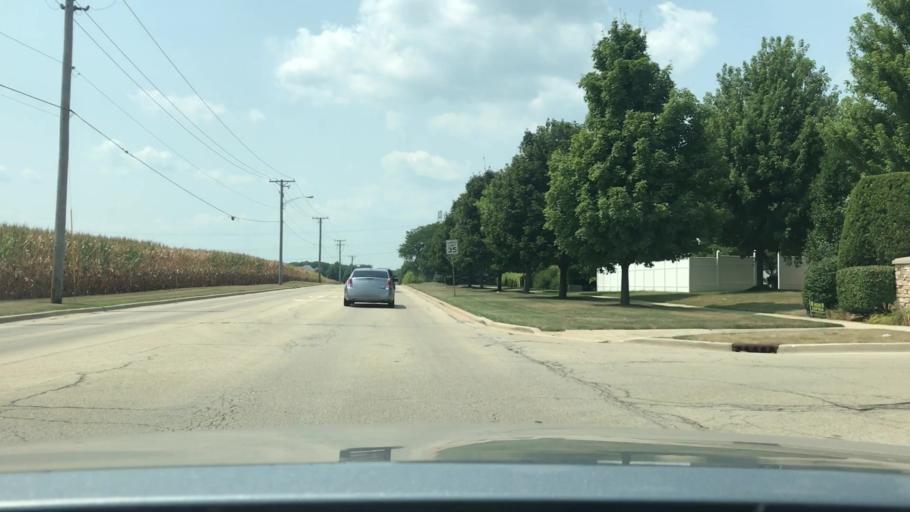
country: US
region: Illinois
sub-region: Will County
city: Plainfield
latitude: 41.5940
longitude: -88.2061
